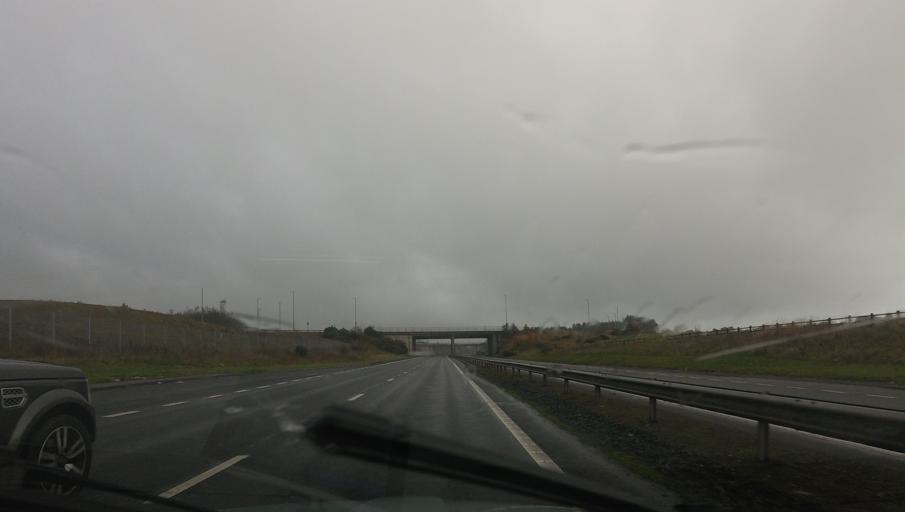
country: GB
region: Scotland
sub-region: Fife
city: Crossgates
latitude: 56.0826
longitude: -3.3886
